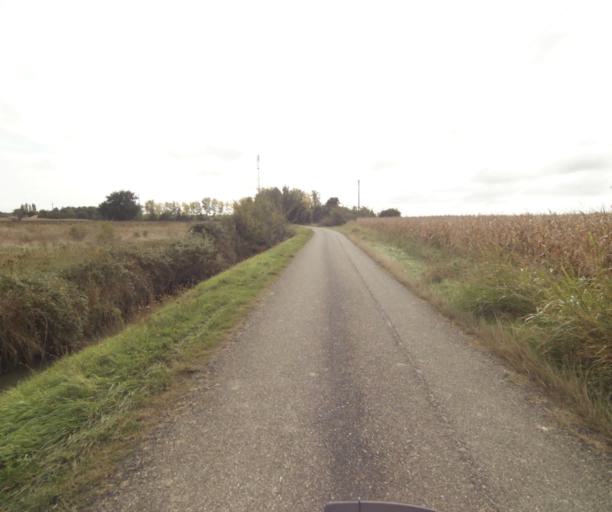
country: FR
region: Midi-Pyrenees
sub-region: Departement du Tarn-et-Garonne
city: Finhan
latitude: 43.9159
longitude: 1.2367
